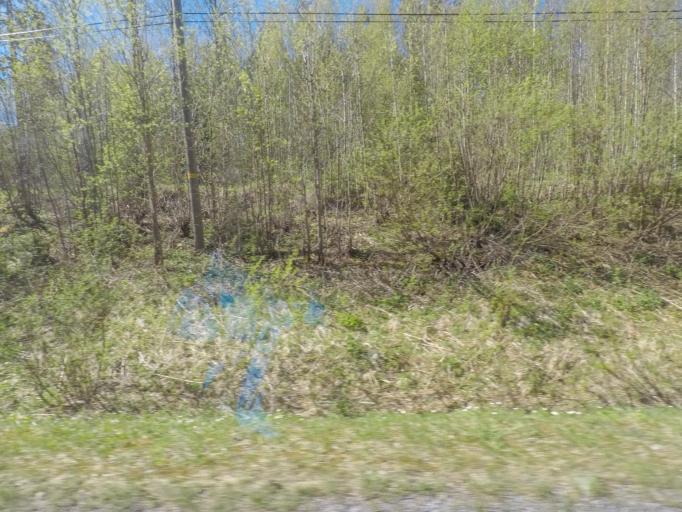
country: FI
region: Uusimaa
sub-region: Helsinki
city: Sammatti
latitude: 60.3711
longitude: 23.8112
